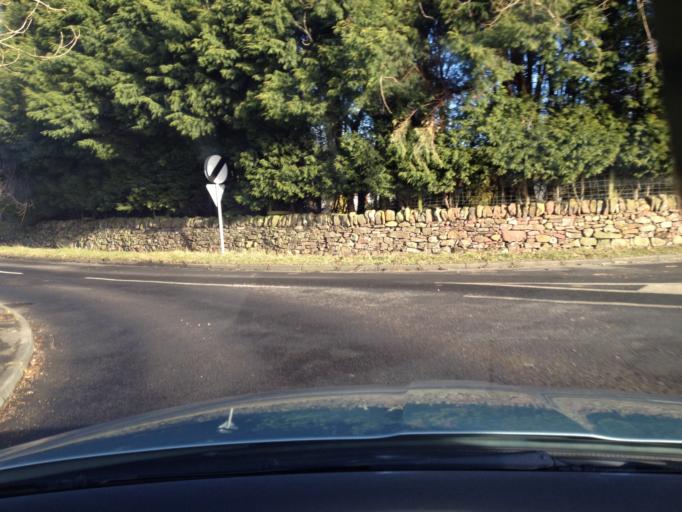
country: GB
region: Scotland
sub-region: Perth and Kinross
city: Milnathort
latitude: 56.2300
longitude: -3.4084
